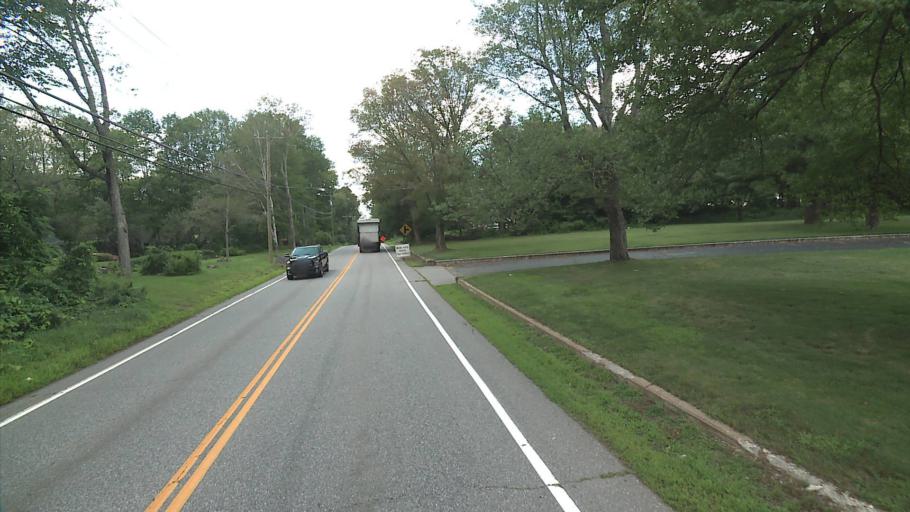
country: US
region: Connecticut
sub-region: Tolland County
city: Stafford Springs
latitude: 41.9530
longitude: -72.2729
